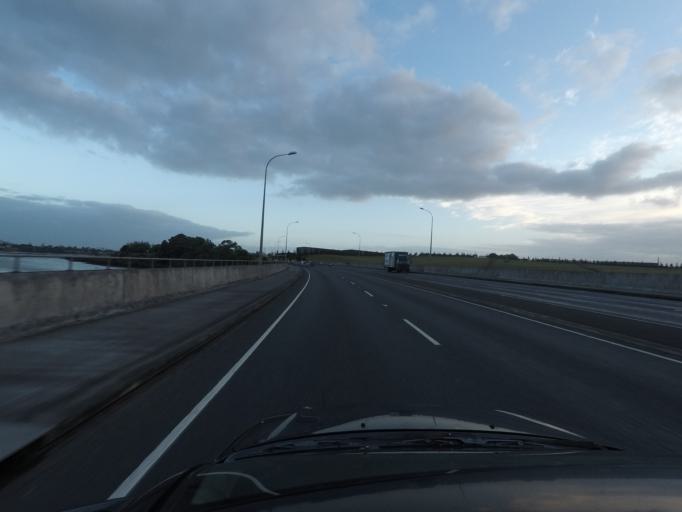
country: NZ
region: Auckland
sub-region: Auckland
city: Manukau City
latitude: -36.9459
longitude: 174.8614
